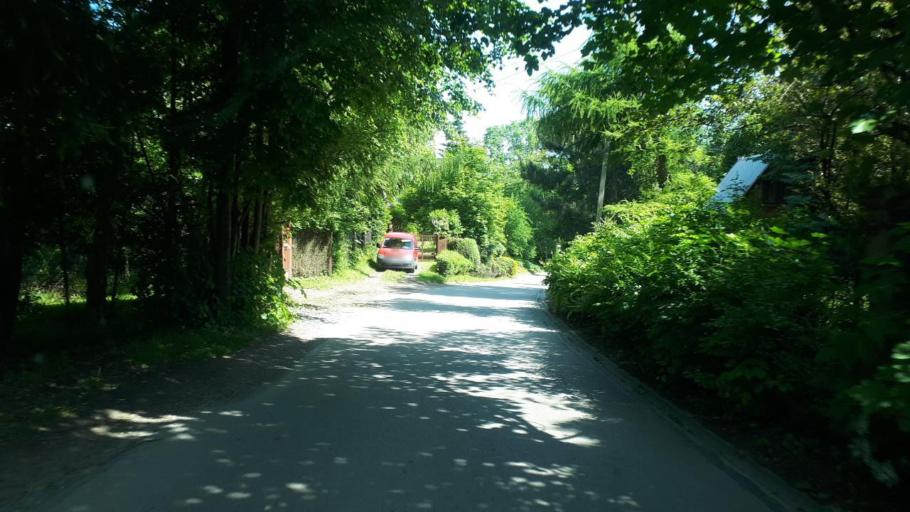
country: PL
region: Silesian Voivodeship
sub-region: Powiat bielski
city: Jaworze
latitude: 49.7887
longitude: 18.9449
